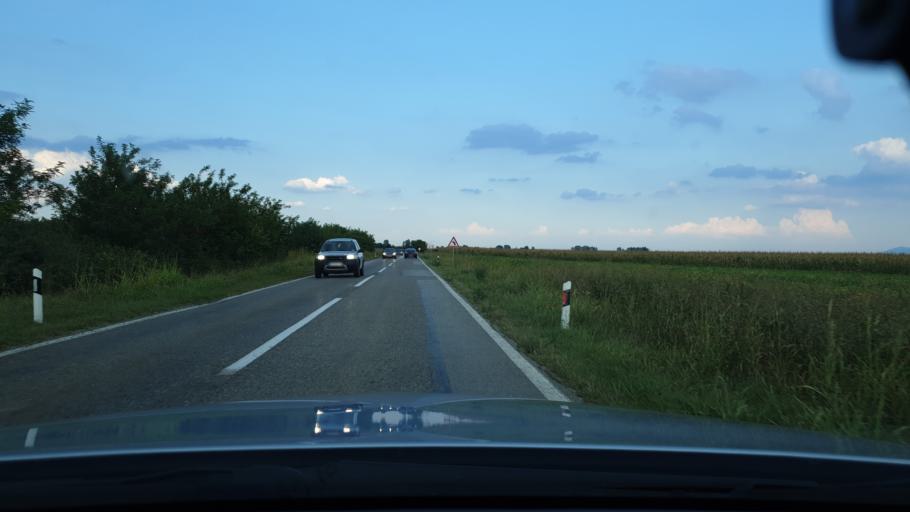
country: RS
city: Velika Greda
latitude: 45.2316
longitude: 21.0051
